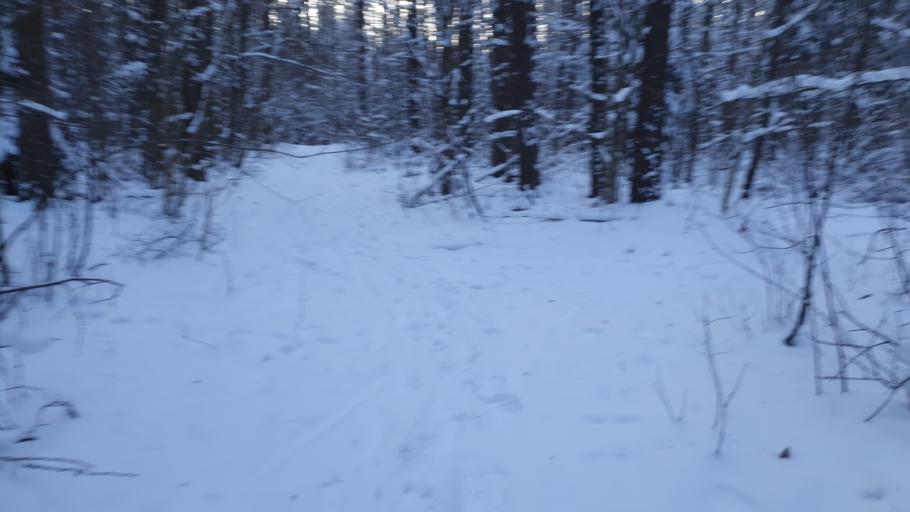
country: LT
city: Skaidiskes
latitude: 54.6457
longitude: 25.4218
